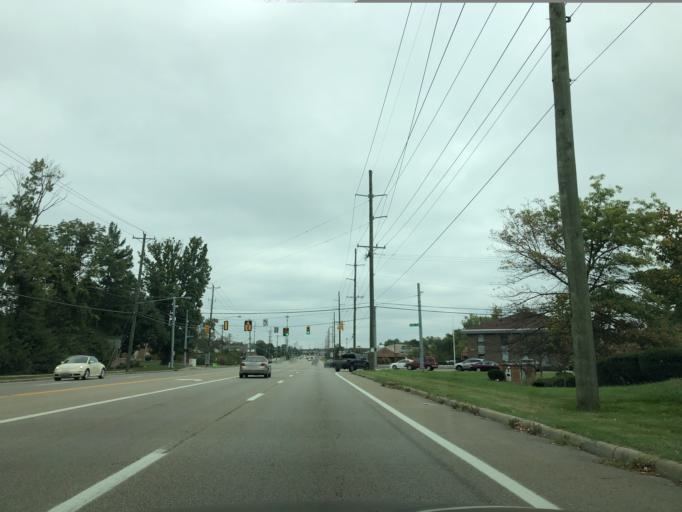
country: US
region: Ohio
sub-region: Hamilton County
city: Sixteen Mile Stand
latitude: 39.2851
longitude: -84.3114
